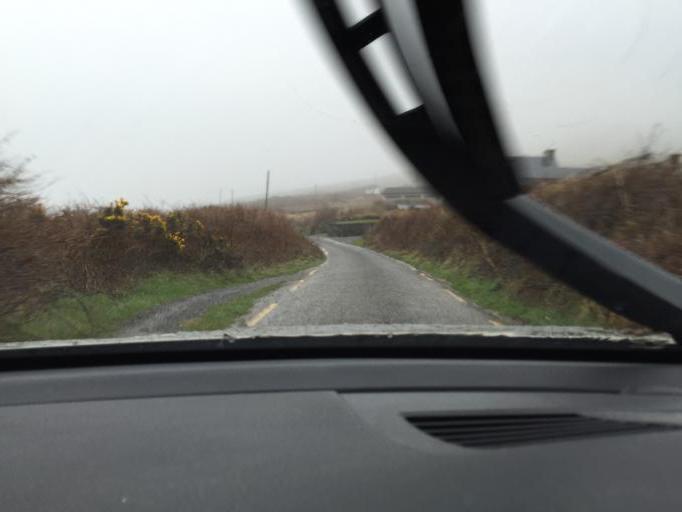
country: IE
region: Munster
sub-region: Ciarrai
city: Dingle
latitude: 52.1323
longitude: -10.4482
